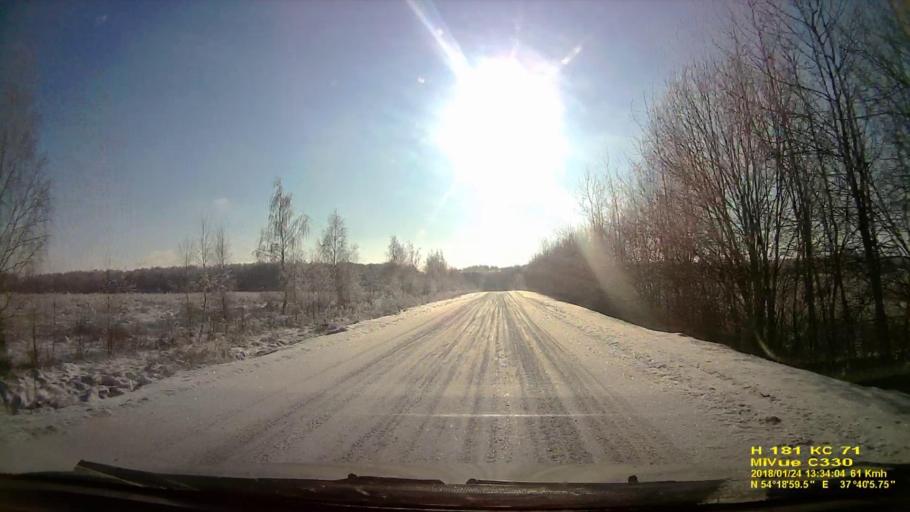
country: RU
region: Tula
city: Revyakino
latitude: 54.3164
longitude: 37.6682
